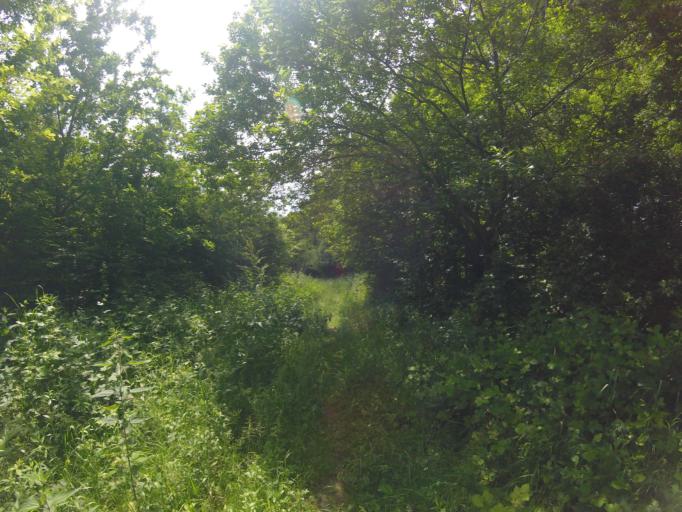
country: HU
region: Veszprem
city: Urkut
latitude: 47.0960
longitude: 17.6477
